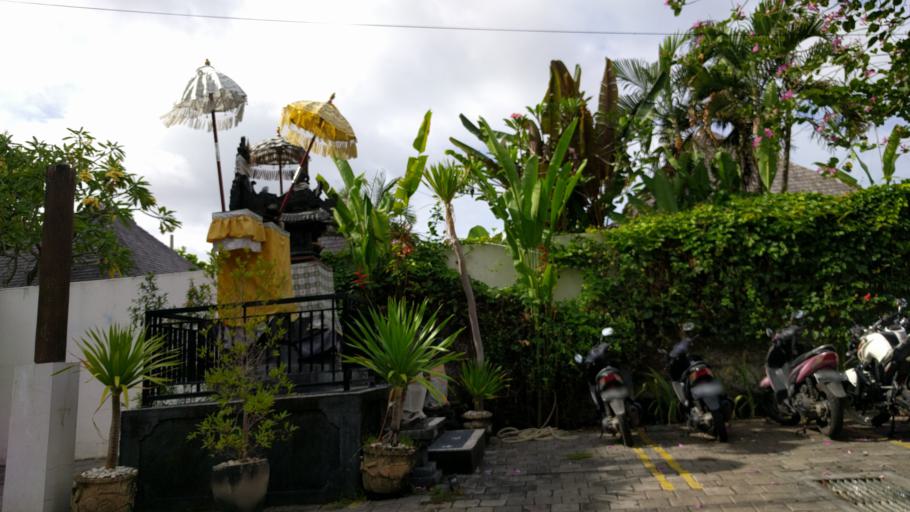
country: ID
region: Bali
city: Kuta
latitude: -8.6815
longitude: 115.1628
